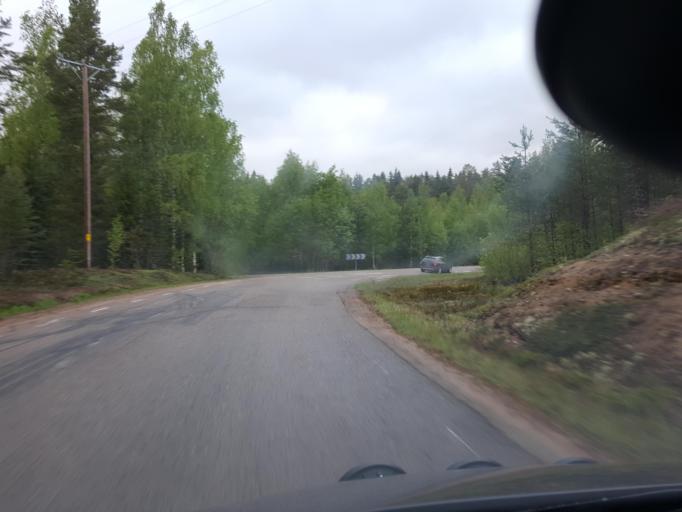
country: SE
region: Gaevleborg
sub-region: Ljusdals Kommun
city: Jaervsoe
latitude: 61.7757
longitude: 16.2122
